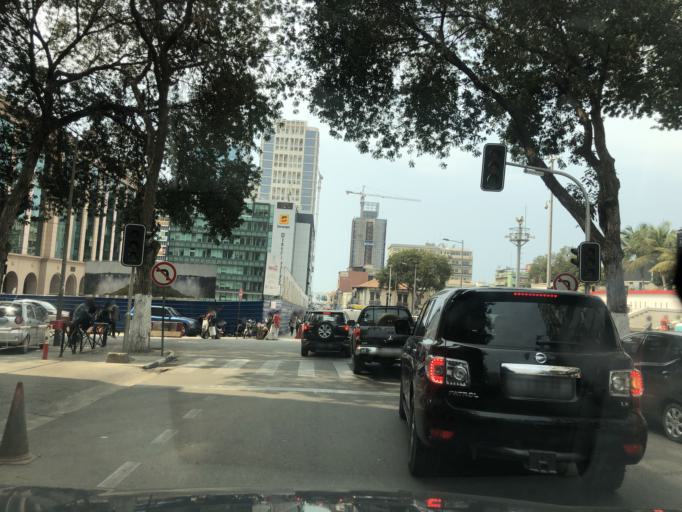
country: AO
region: Luanda
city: Luanda
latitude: -8.8157
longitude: 13.2321
